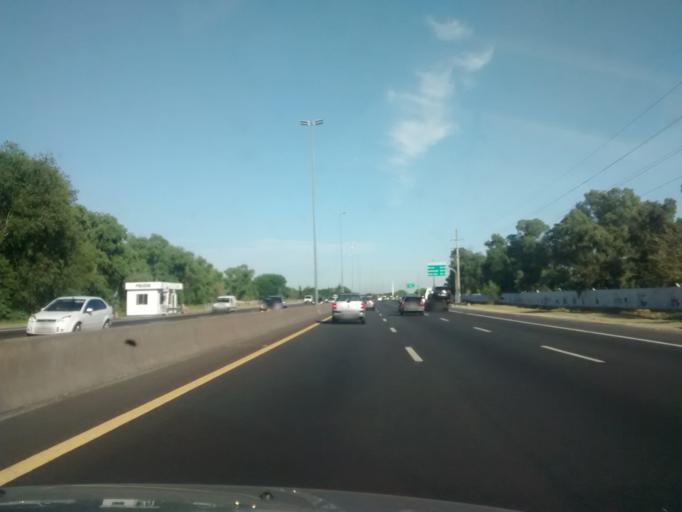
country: AR
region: Buenos Aires
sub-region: Partido de Quilmes
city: Quilmes
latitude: -34.7107
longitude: -58.2539
